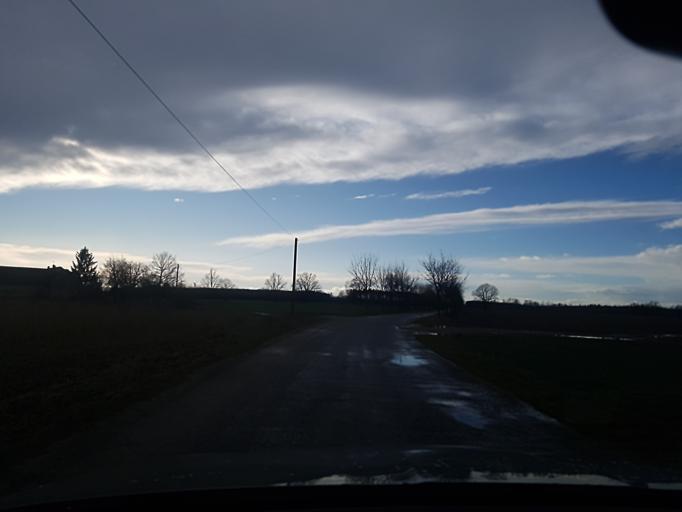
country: DE
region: Brandenburg
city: Falkenberg
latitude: 51.6115
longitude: 13.2935
